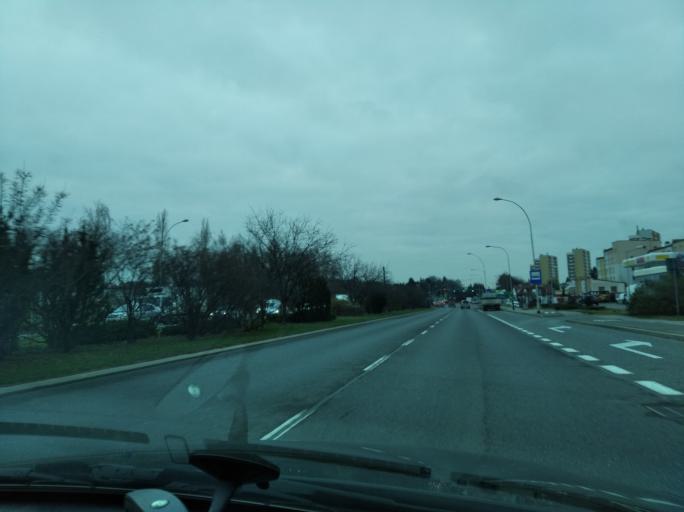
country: PL
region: Subcarpathian Voivodeship
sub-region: Rzeszow
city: Rzeszow
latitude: 50.0283
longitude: 21.9766
